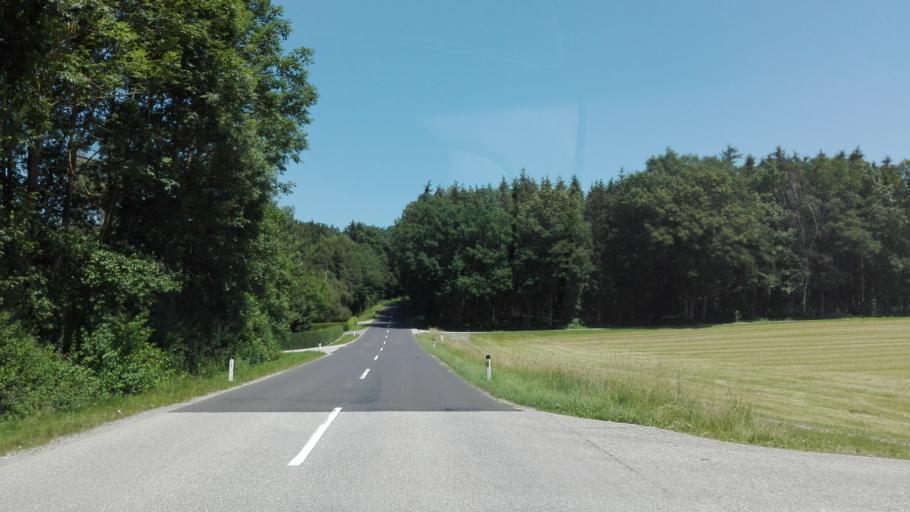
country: AT
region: Upper Austria
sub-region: Politischer Bezirk Grieskirchen
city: Grieskirchen
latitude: 48.3602
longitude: 13.8644
